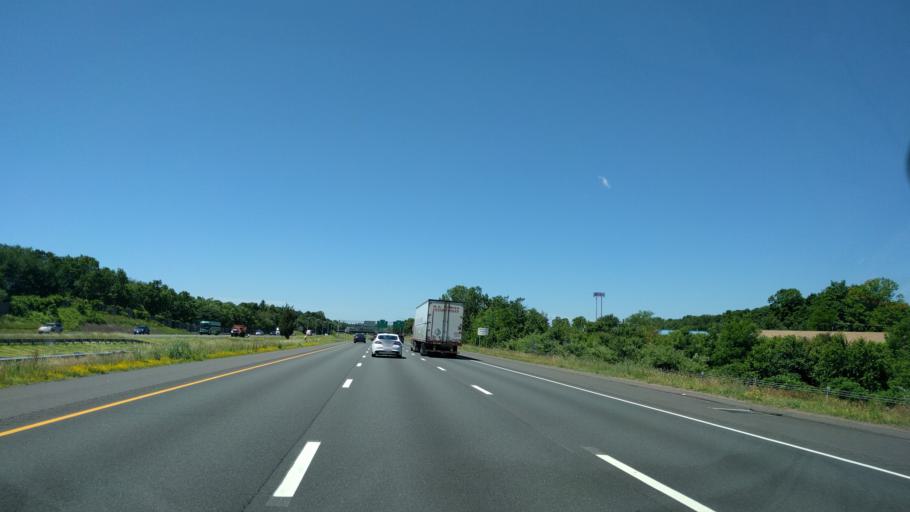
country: US
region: Connecticut
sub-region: Tolland County
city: Rockville
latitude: 41.8295
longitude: -72.4754
